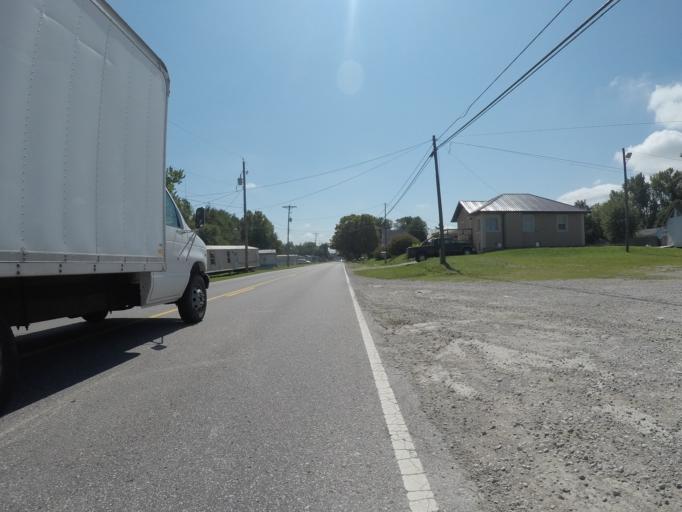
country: US
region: Kentucky
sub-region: Boyd County
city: Ashland
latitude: 38.4694
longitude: -82.6055
